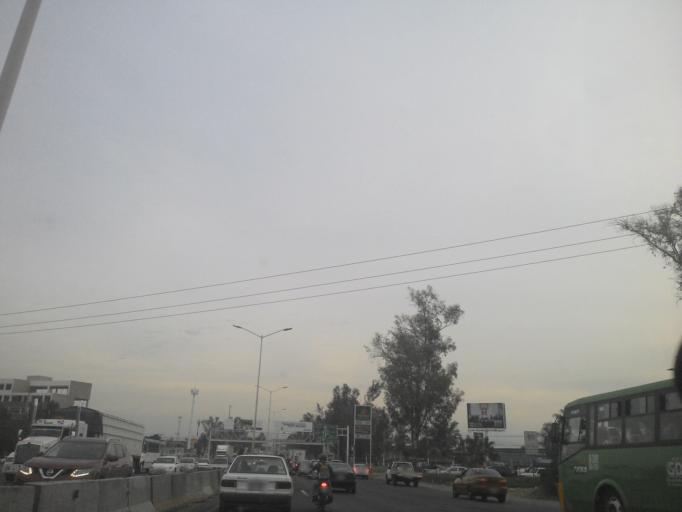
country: MX
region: Jalisco
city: Guadalajara
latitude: 20.6505
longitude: -103.4443
